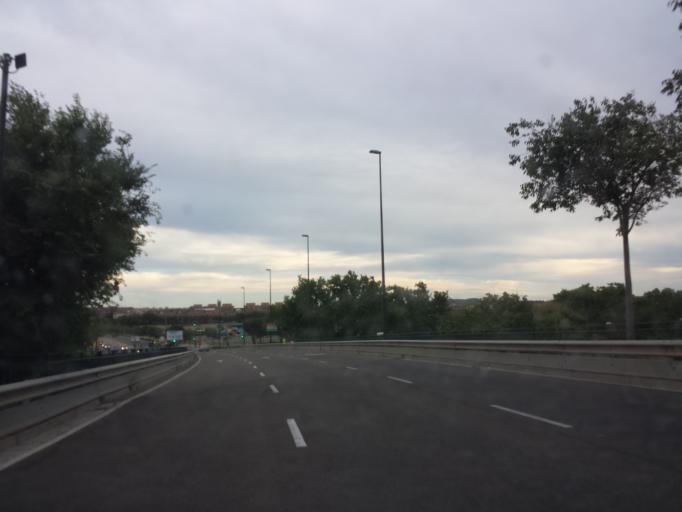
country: ES
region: Aragon
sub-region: Provincia de Zaragoza
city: Oliver-Valdefierro, Oliver, Valdefierro
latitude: 41.6358
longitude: -0.9236
